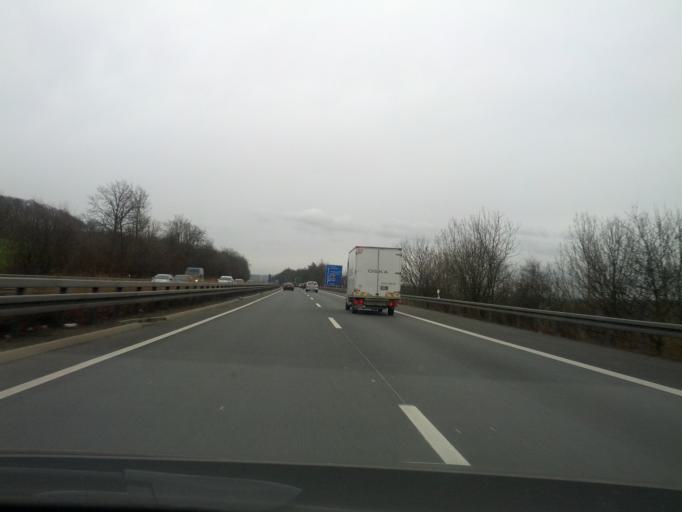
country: DE
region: Lower Saxony
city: Holle
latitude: 52.1100
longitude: 10.1341
